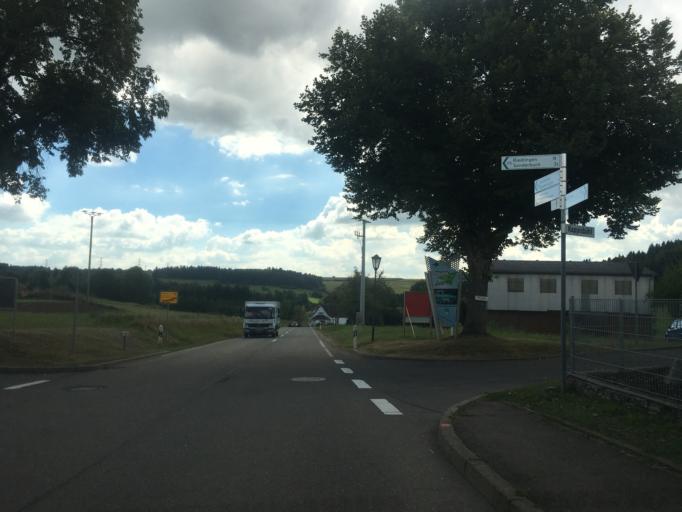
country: DE
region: Baden-Wuerttemberg
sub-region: Tuebingen Region
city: Hayingen
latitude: 48.2723
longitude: 9.4752
